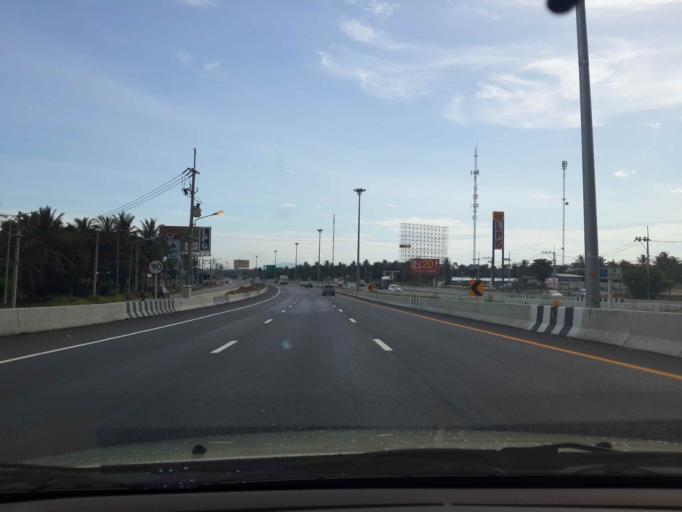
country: TH
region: Chon Buri
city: Ban Talat Bueng
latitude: 13.0096
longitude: 100.9957
